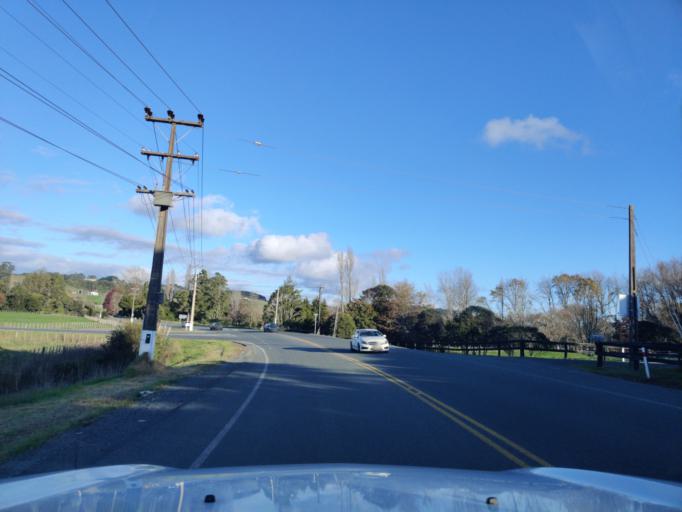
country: NZ
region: Auckland
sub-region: Auckland
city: Red Hill
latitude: -36.9826
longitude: 174.9911
